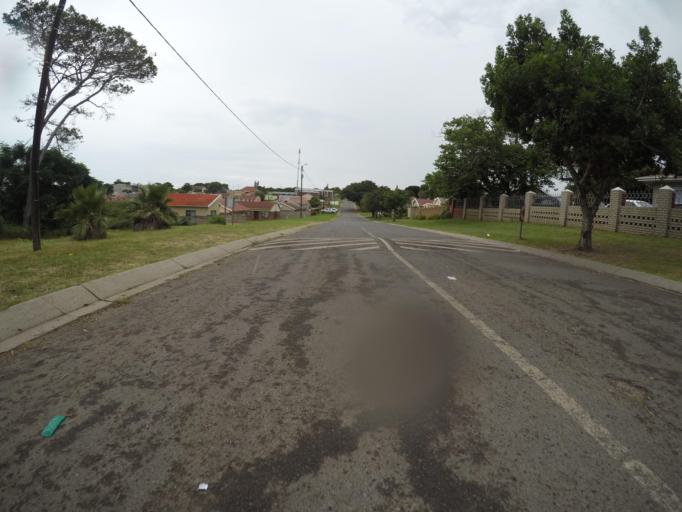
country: ZA
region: Eastern Cape
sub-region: Buffalo City Metropolitan Municipality
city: East London
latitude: -32.9678
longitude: 27.8342
